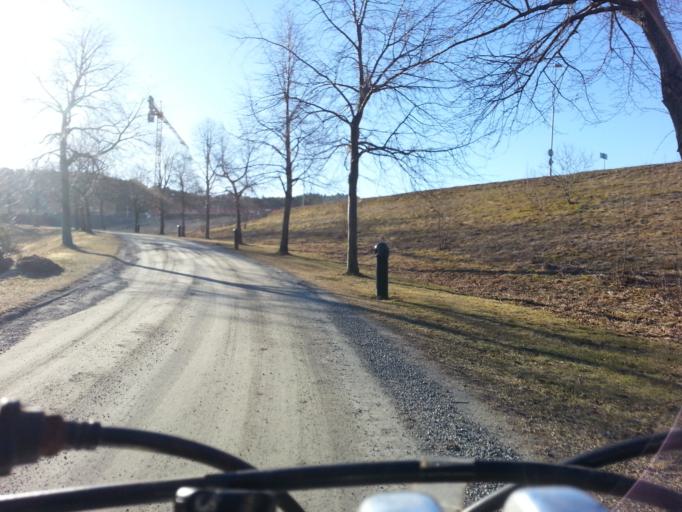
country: NO
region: Sor-Trondelag
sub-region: Trondheim
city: Trondheim
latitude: 63.4376
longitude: 10.4710
